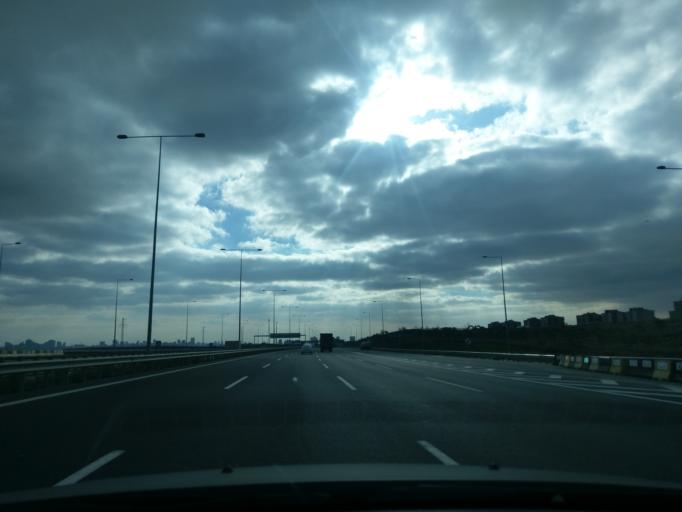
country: TR
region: Istanbul
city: Basaksehir
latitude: 41.1126
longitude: 28.8153
